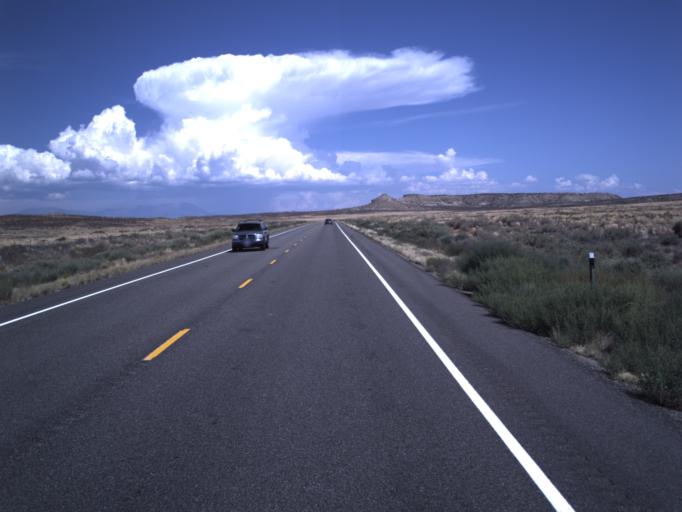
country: US
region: Utah
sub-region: San Juan County
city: Blanding
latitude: 37.3258
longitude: -109.5217
